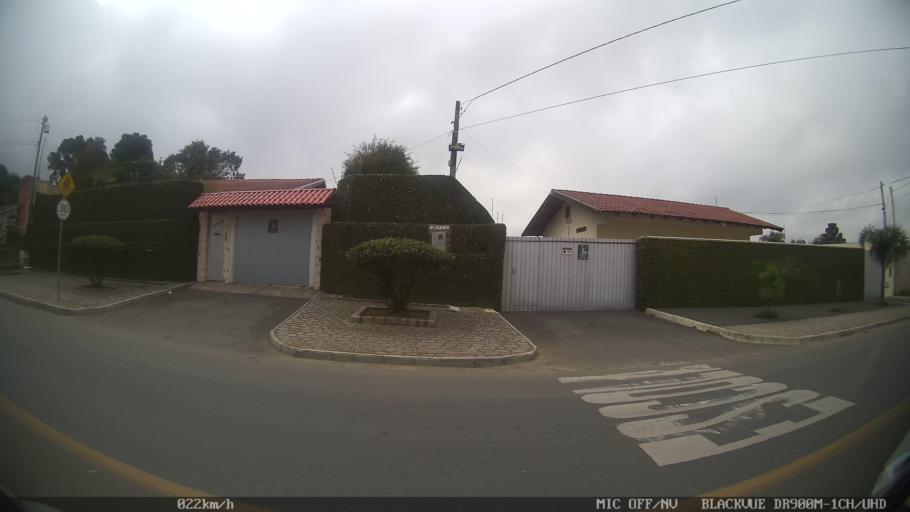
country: BR
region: Parana
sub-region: Almirante Tamandare
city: Almirante Tamandare
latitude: -25.3534
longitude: -49.2711
